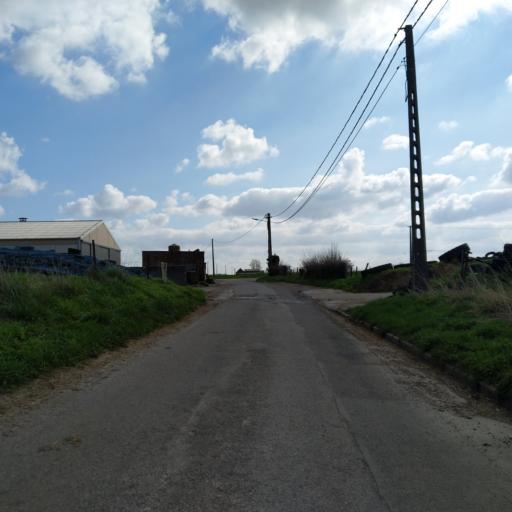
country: BE
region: Wallonia
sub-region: Province du Hainaut
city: Jurbise
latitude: 50.5568
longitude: 3.9416
